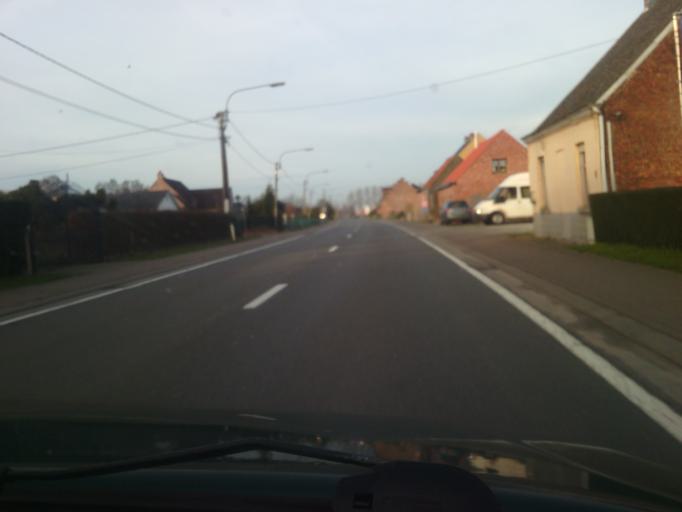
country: BE
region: Flanders
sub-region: Provincie Oost-Vlaanderen
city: Laarne
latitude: 51.0530
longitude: 3.8813
